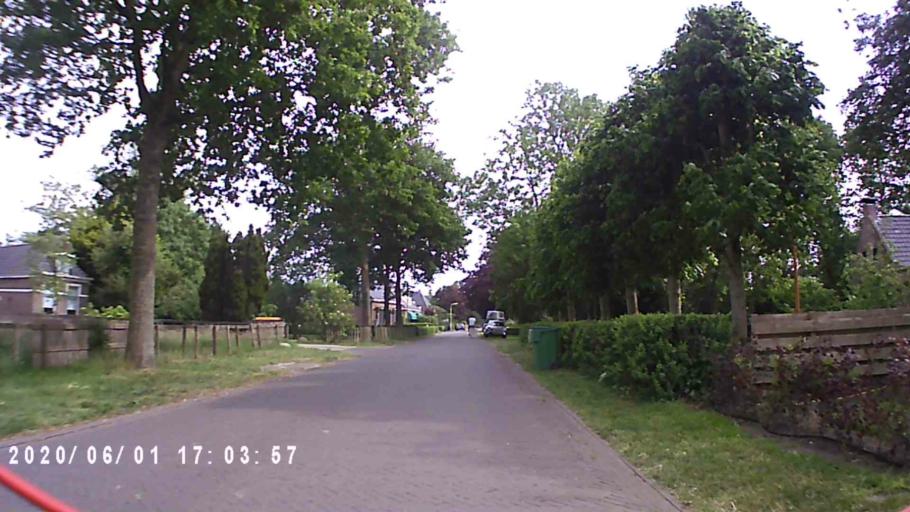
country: NL
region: Friesland
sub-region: Gemeente Tytsjerksteradiel
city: Garyp
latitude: 53.1758
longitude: 5.9326
